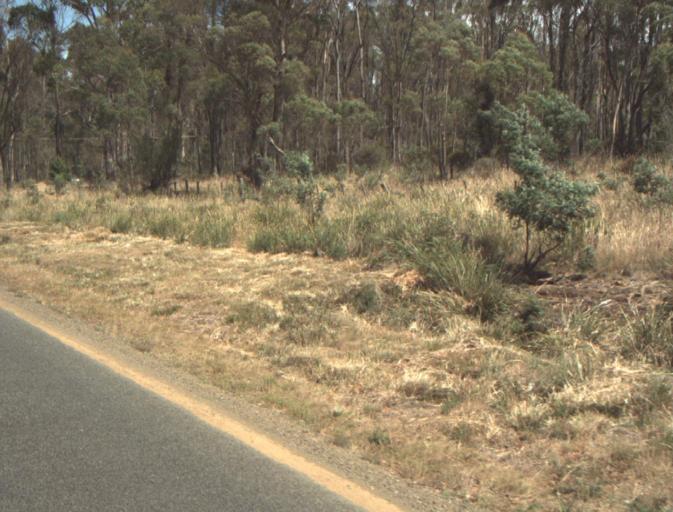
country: AU
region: Tasmania
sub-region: Launceston
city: Mayfield
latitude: -41.3314
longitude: 147.1406
